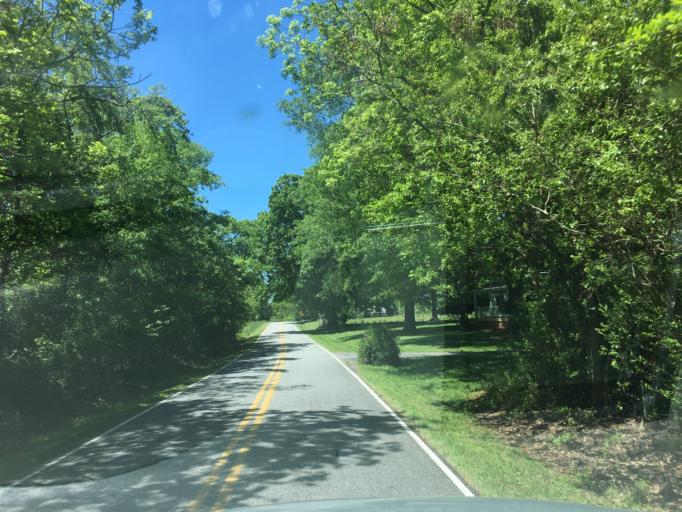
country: US
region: South Carolina
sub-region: Spartanburg County
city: Duncan
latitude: 34.8703
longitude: -82.1760
